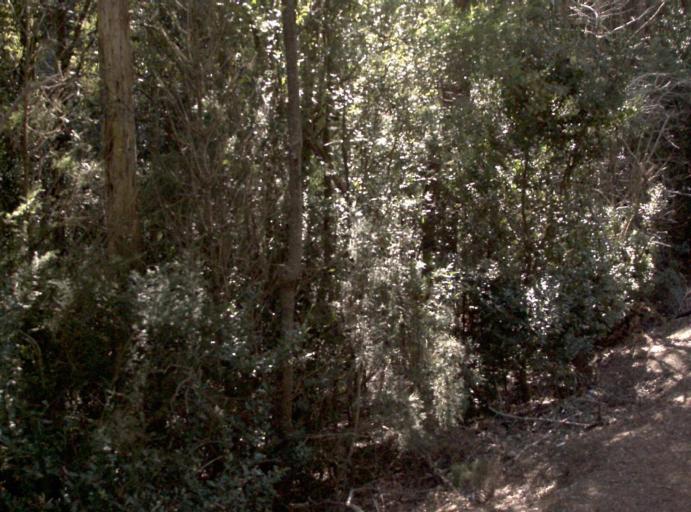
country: AU
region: Tasmania
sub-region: Launceston
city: Mayfield
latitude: -41.2993
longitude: 147.2000
